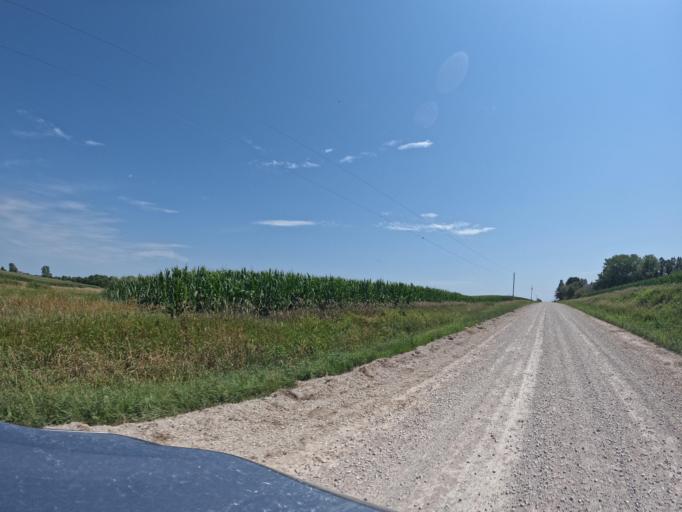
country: US
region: Iowa
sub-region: Henry County
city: Mount Pleasant
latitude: 40.8965
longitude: -91.6317
